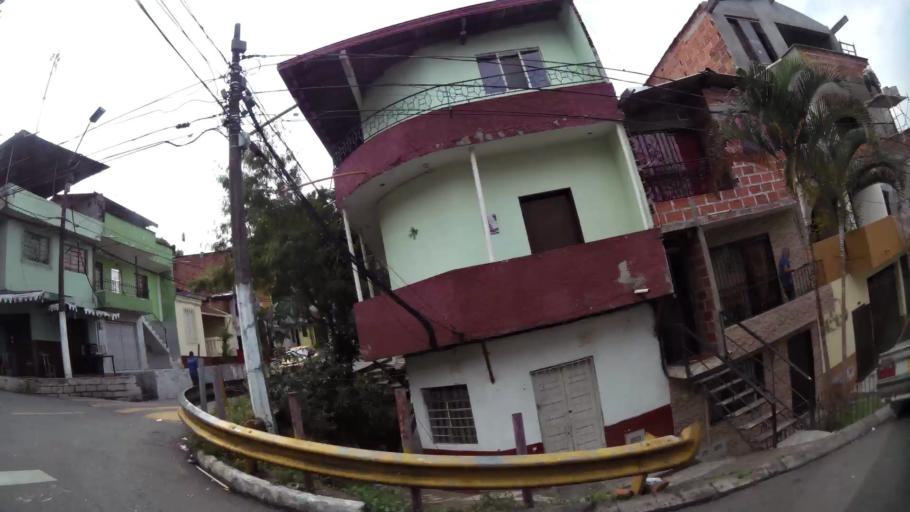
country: CO
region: Antioquia
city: Medellin
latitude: 6.2736
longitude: -75.5498
